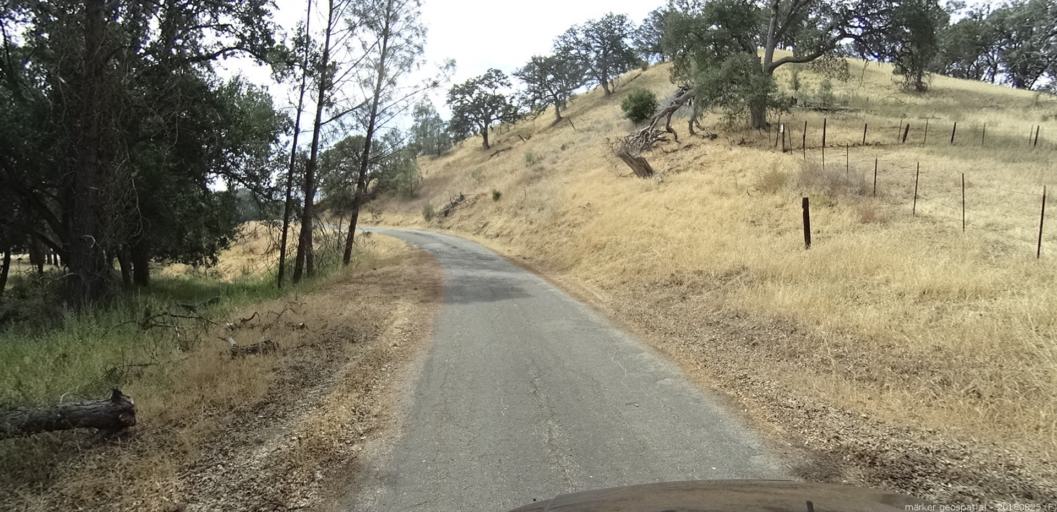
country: US
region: California
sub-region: Fresno County
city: Coalinga
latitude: 36.1836
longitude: -120.6807
